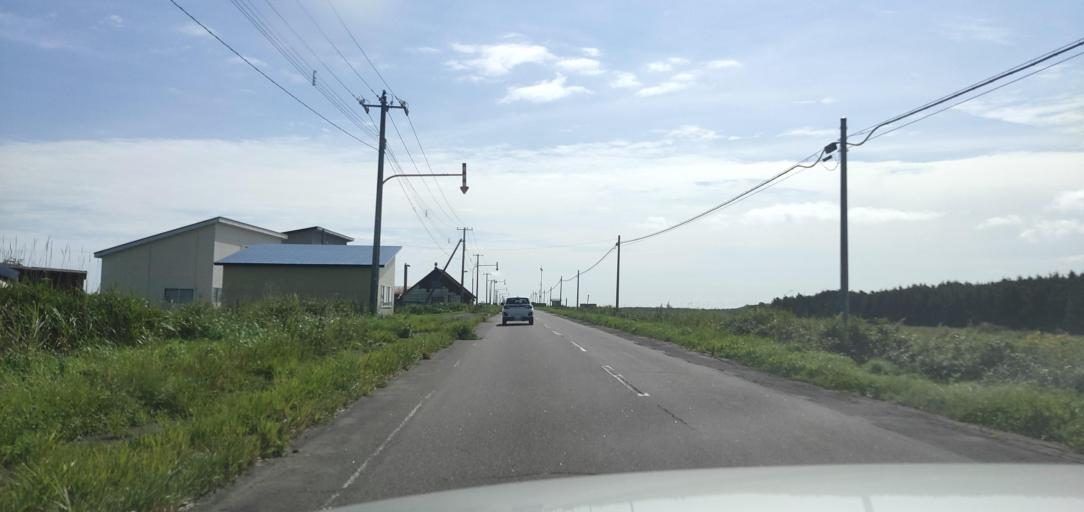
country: JP
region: Hokkaido
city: Shibetsu
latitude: 43.6354
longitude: 145.1742
